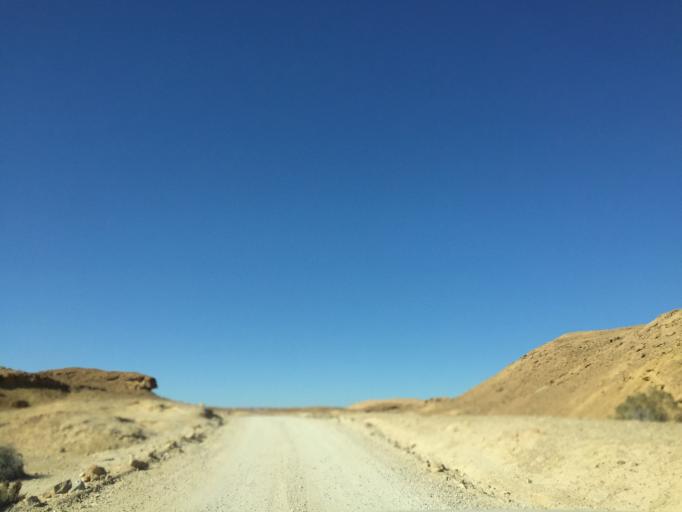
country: IL
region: Southern District
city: Mitzpe Ramon
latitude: 30.6078
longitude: 34.9378
